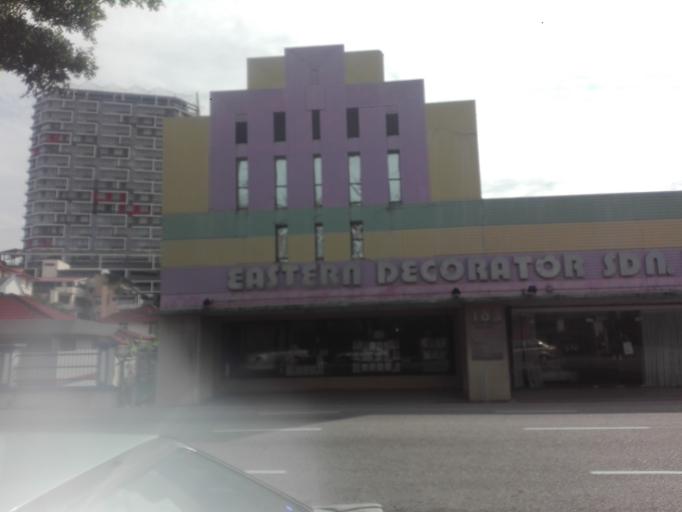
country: MY
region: Perak
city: Ipoh
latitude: 4.5927
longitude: 101.0854
